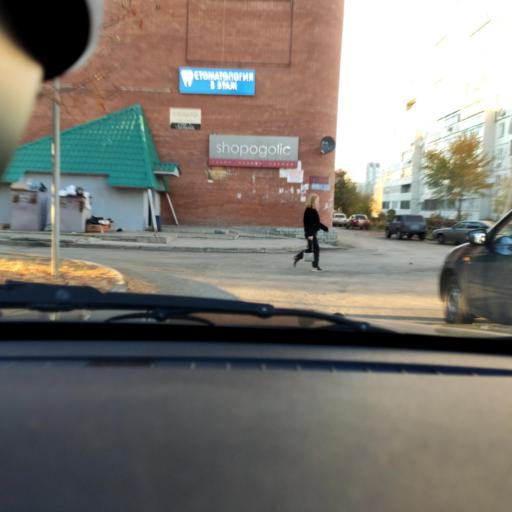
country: RU
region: Samara
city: Tol'yatti
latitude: 53.5459
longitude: 49.3286
